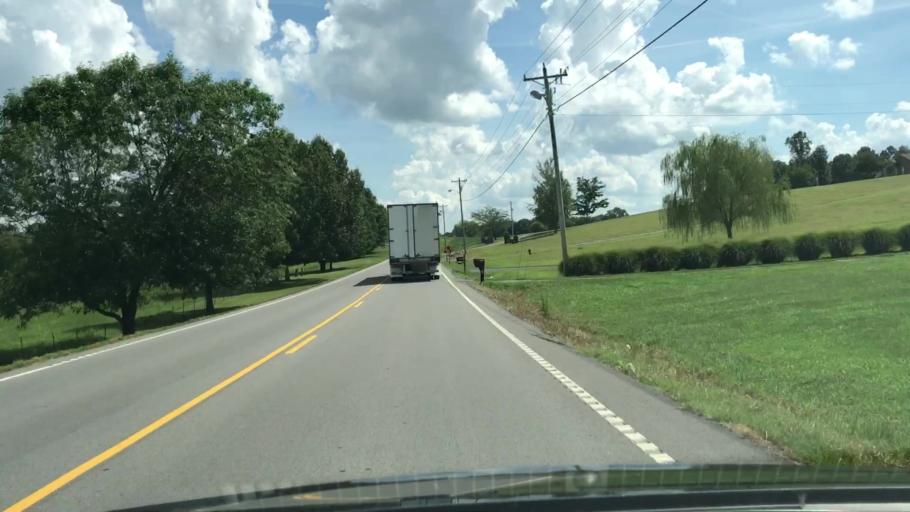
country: US
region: Tennessee
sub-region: Robertson County
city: Cross Plains
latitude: 36.5397
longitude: -86.6670
